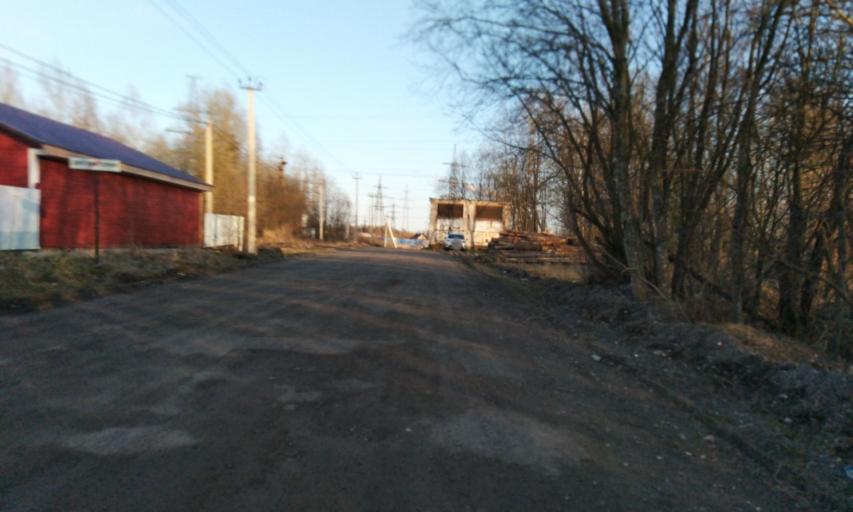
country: RU
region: Leningrad
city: Novoye Devyatkino
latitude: 60.0915
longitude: 30.4585
